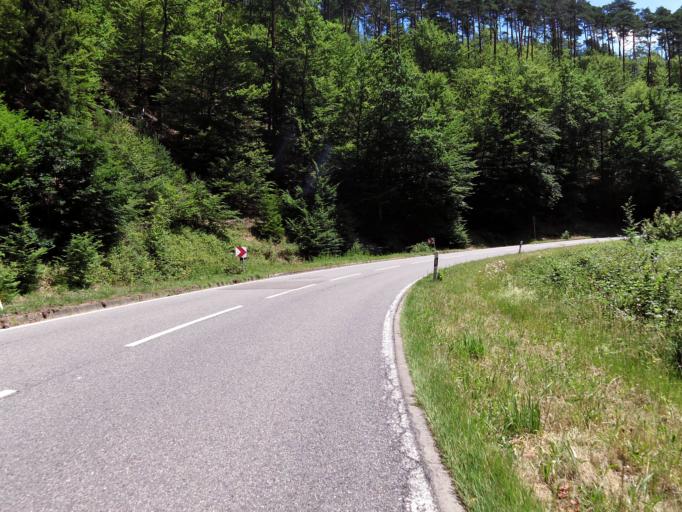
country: DE
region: Rheinland-Pfalz
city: Elmstein
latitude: 49.3608
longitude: 7.9093
